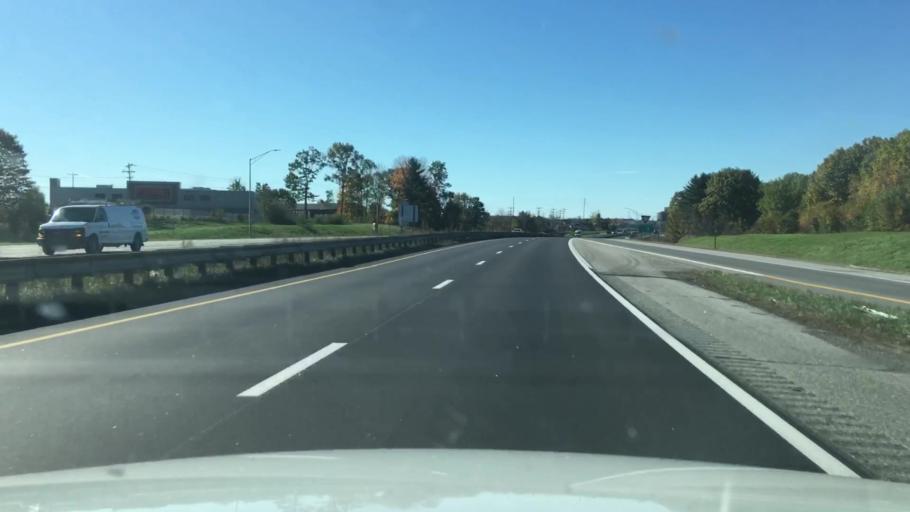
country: US
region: Maine
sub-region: Cumberland County
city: South Portland Gardens
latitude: 43.6457
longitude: -70.3322
